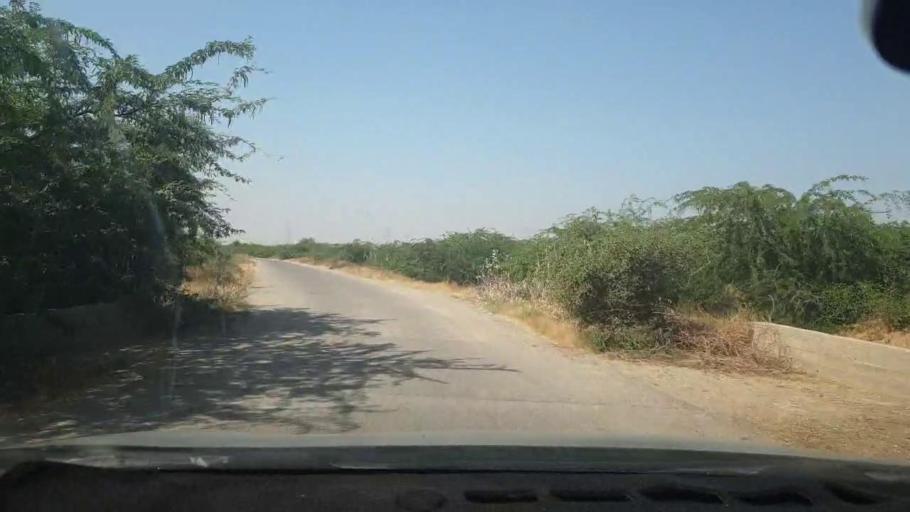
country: PK
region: Sindh
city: Malir Cantonment
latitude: 25.1574
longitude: 67.1427
